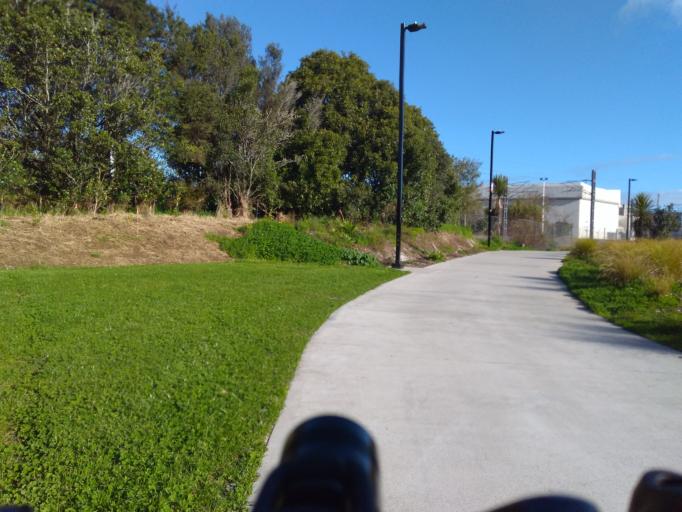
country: NZ
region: Auckland
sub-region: Auckland
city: Rosebank
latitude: -36.8911
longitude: 174.7068
